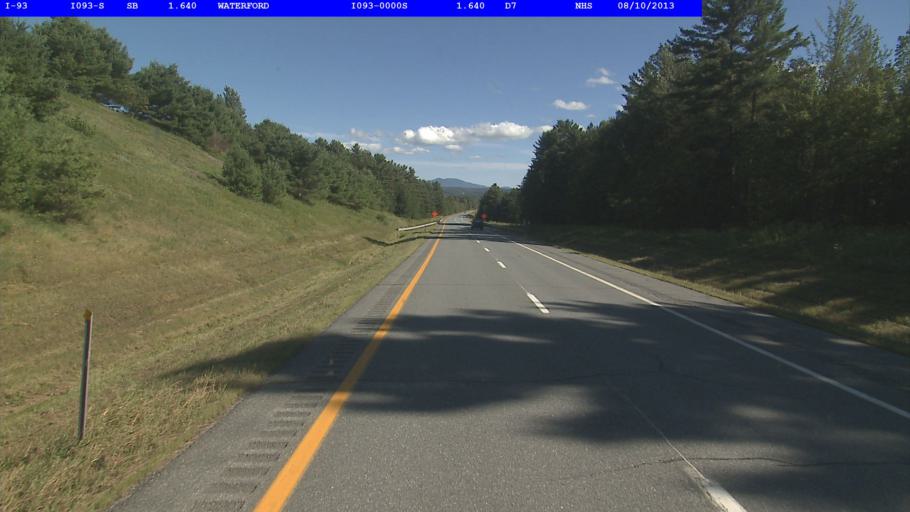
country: US
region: Vermont
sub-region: Caledonia County
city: Saint Johnsbury
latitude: 44.3654
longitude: -71.9027
